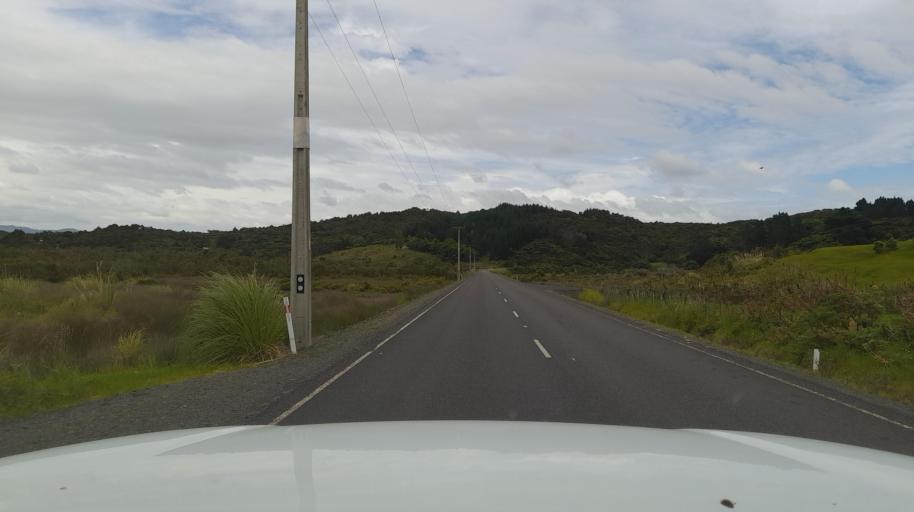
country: NZ
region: Northland
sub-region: Far North District
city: Kaitaia
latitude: -35.4035
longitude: 173.3821
